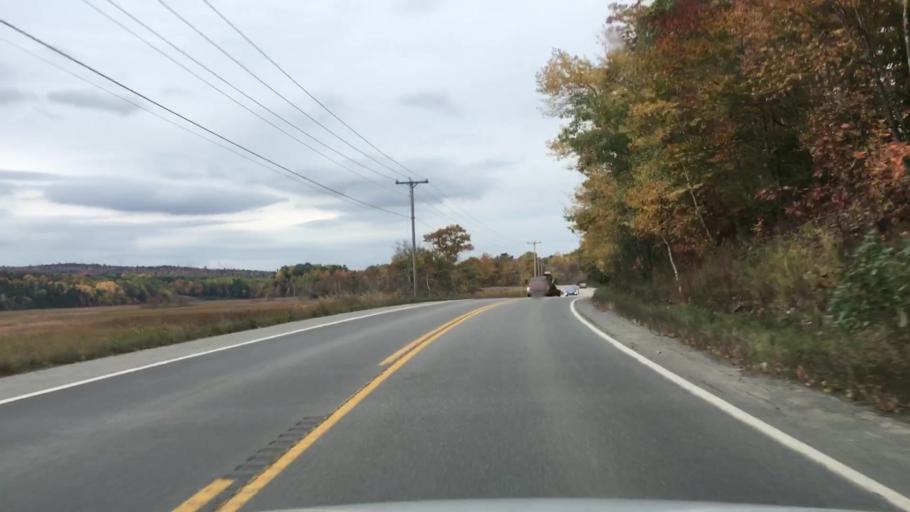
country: US
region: Maine
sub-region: Waldo County
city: Frankfort
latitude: 44.5853
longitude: -68.8636
